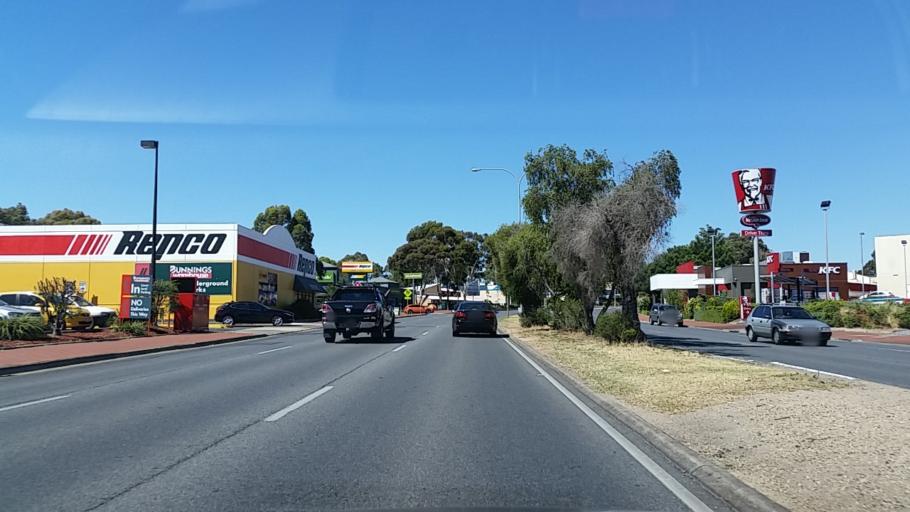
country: AU
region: South Australia
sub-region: Tea Tree Gully
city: Modbury
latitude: -34.8328
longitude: 138.6839
